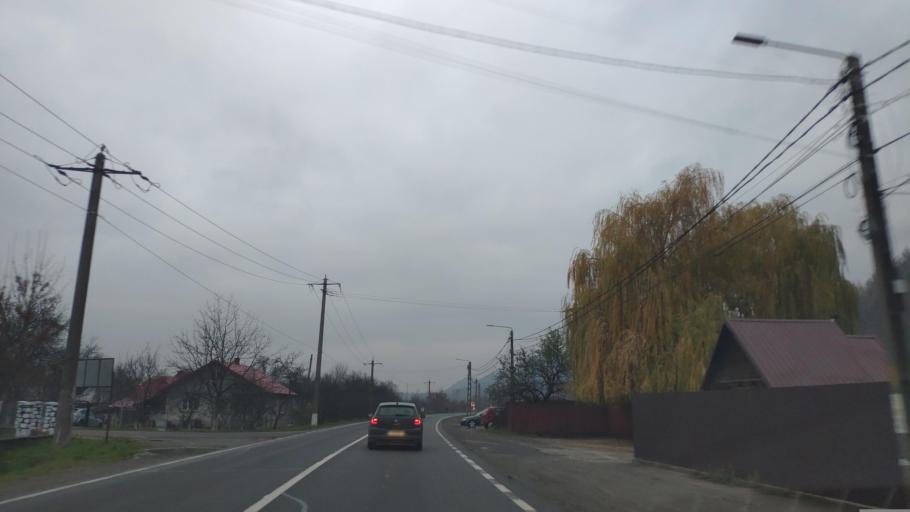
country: RO
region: Maramures
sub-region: Comuna Cicarlau
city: Ilba
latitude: 47.7166
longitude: 23.3459
